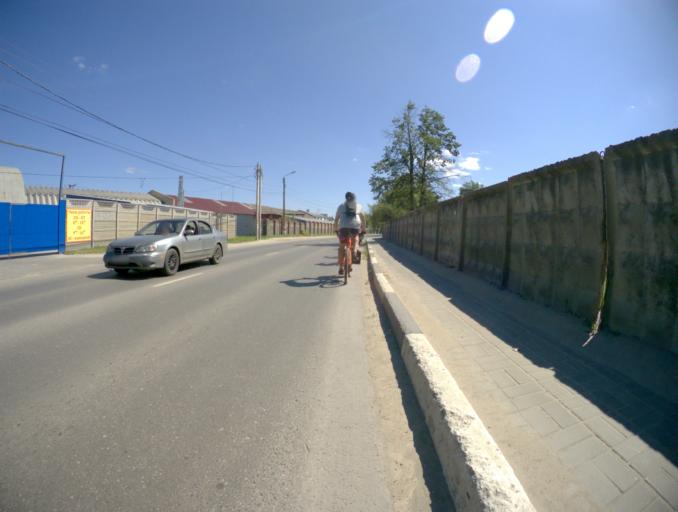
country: RU
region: Nizjnij Novgorod
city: Bor
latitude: 56.3604
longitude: 44.0678
